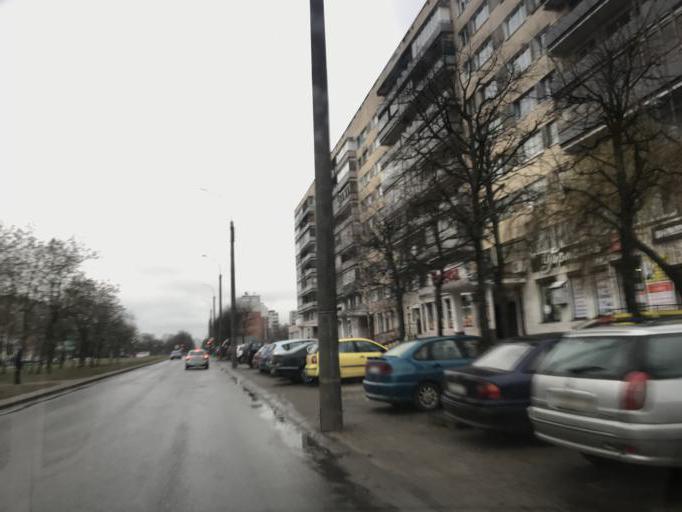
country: BY
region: Mogilev
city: Mahilyow
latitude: 53.8758
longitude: 30.3291
